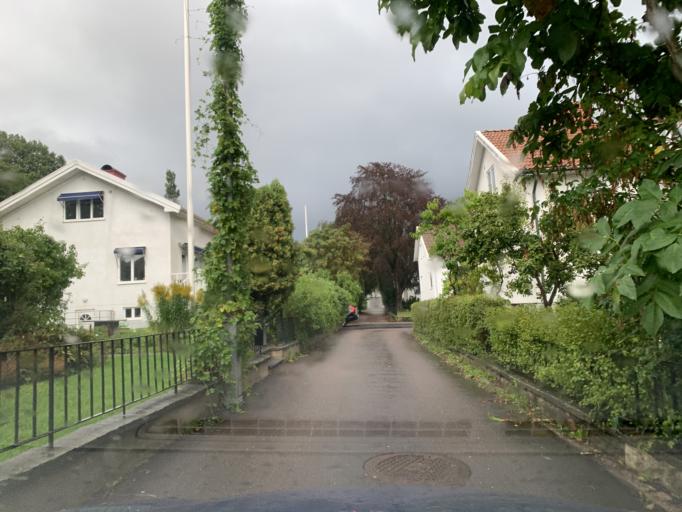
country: SE
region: Vaestra Goetaland
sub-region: Goteborg
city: Goeteborg
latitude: 57.7048
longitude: 12.0158
